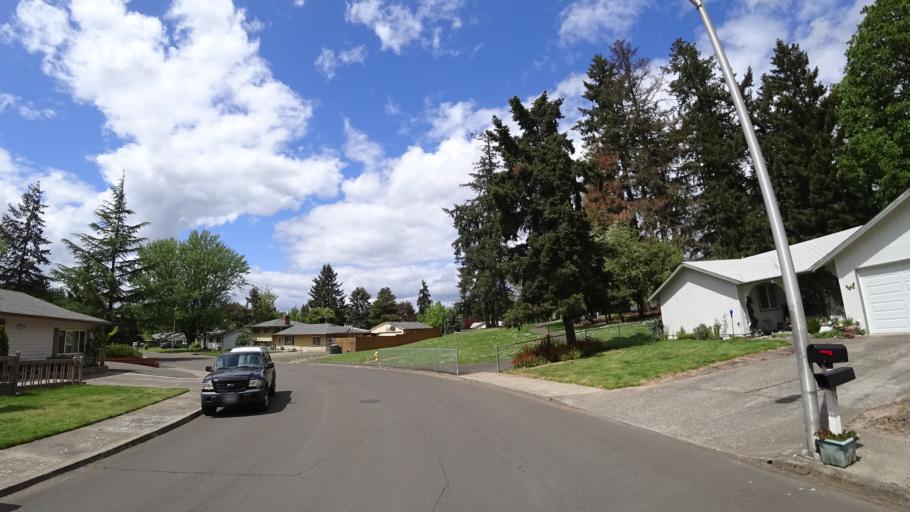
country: US
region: Oregon
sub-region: Washington County
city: Aloha
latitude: 45.4745
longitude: -122.8559
